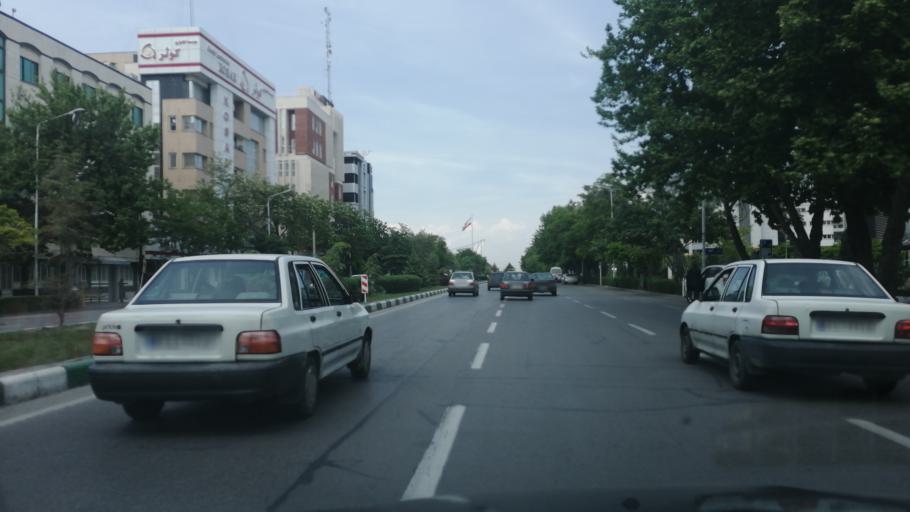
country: IR
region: Razavi Khorasan
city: Mashhad
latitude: 36.3205
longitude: 59.5663
